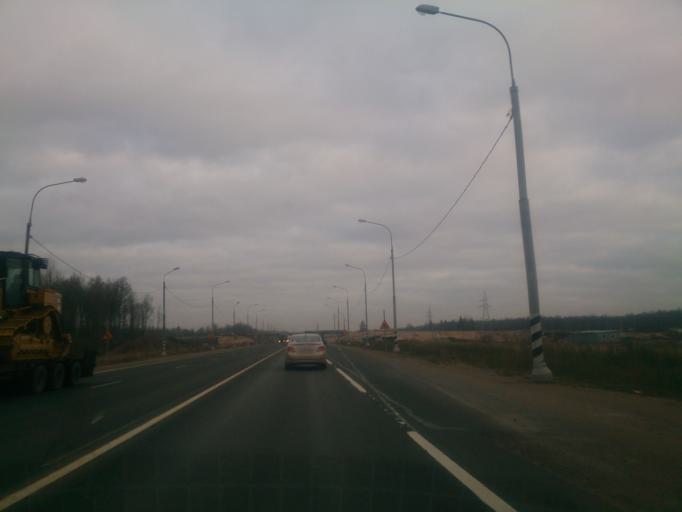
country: RU
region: Novgorod
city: Krechevitsy
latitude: 58.8014
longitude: 31.4614
